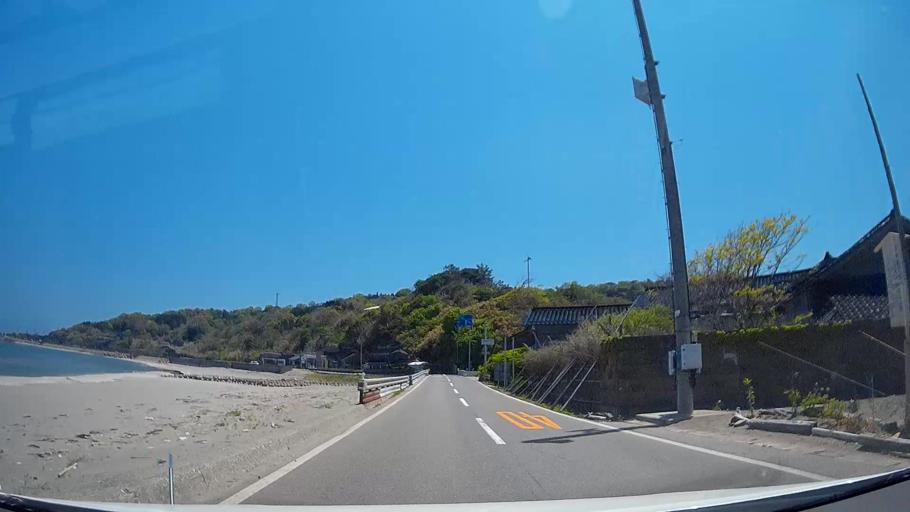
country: JP
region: Ishikawa
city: Nanao
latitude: 37.5271
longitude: 137.2815
